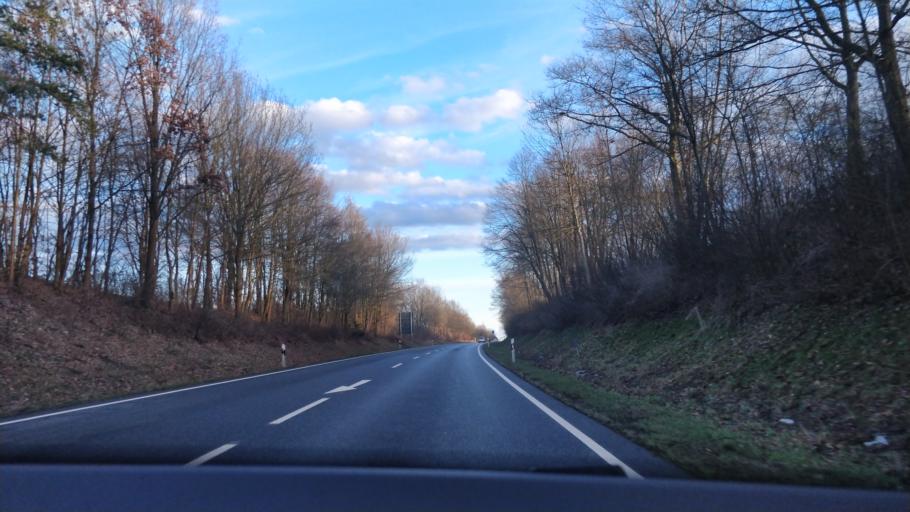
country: DE
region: Bavaria
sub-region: Upper Palatinate
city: Pressath
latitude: 49.7597
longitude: 11.9260
